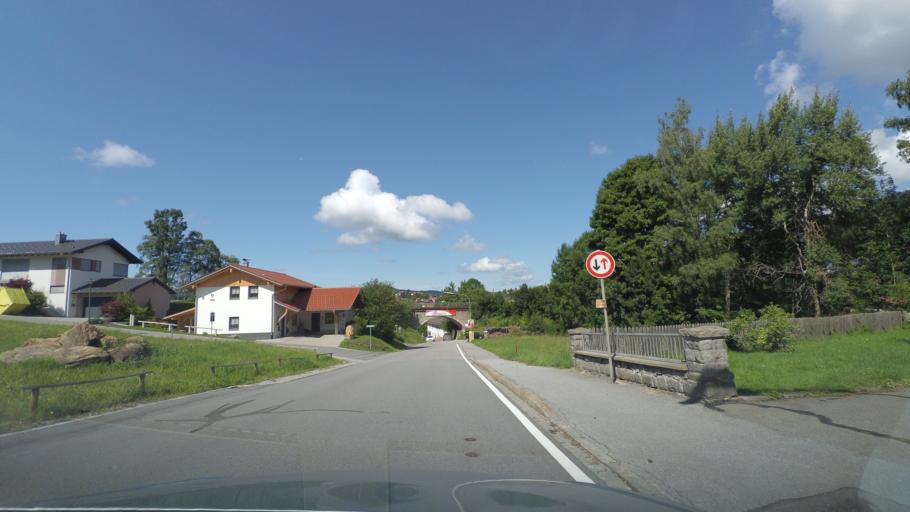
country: DE
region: Bavaria
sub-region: Lower Bavaria
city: Bodenmais
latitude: 49.0675
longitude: 13.1090
